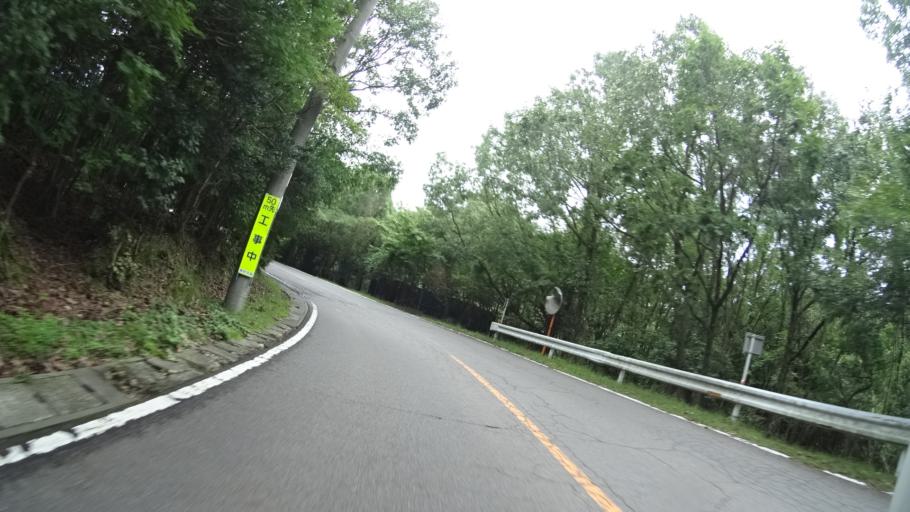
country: JP
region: Oita
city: Beppu
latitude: 33.2943
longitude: 131.3729
